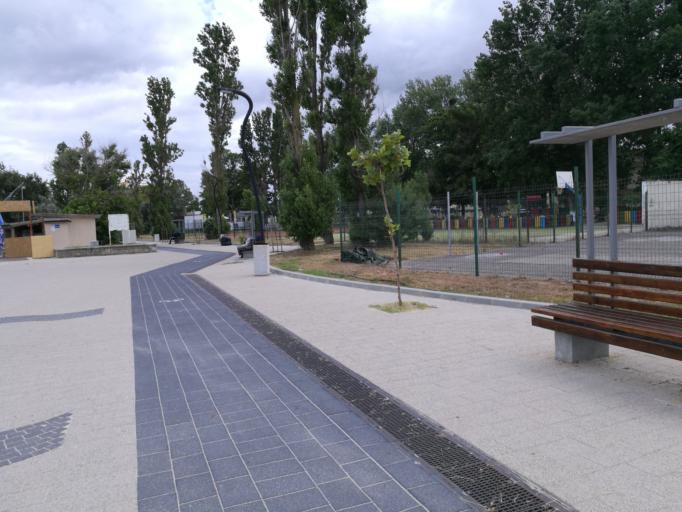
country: RO
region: Constanta
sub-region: Municipiul Constanta
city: Palazu Mare
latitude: 44.2505
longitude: 28.6221
